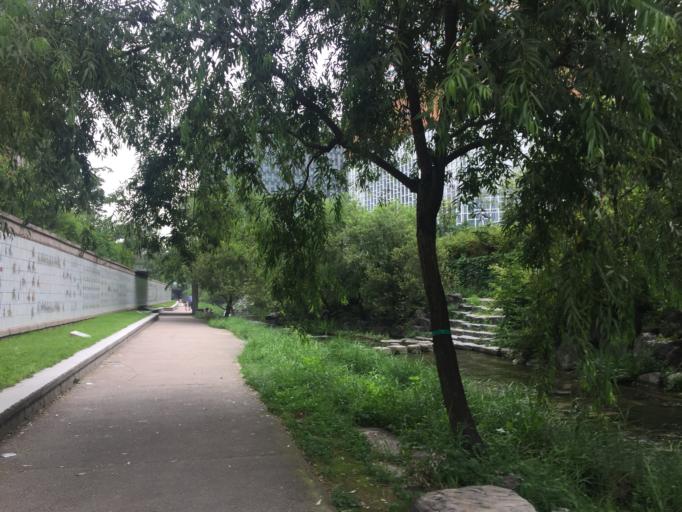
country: KR
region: Seoul
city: Seoul
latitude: 37.5685
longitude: 126.9851
